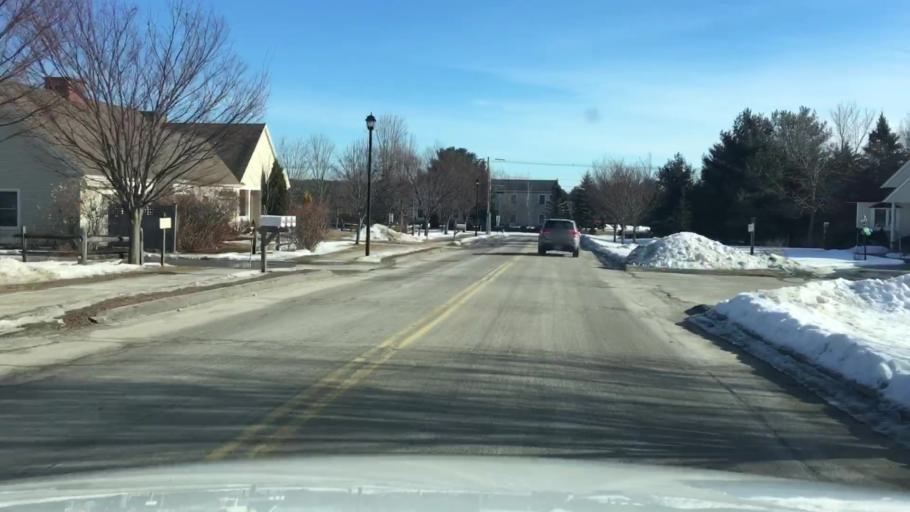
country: US
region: Maine
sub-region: Cumberland County
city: Falmouth
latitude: 43.7207
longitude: -70.2498
